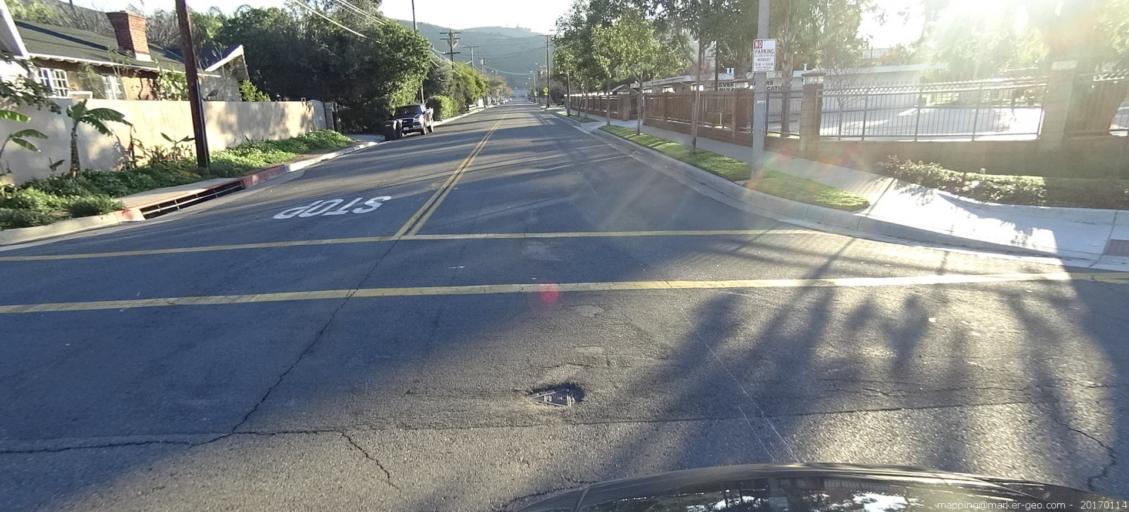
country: US
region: California
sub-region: Orange County
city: Villa Park
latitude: 33.7950
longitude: -117.8057
